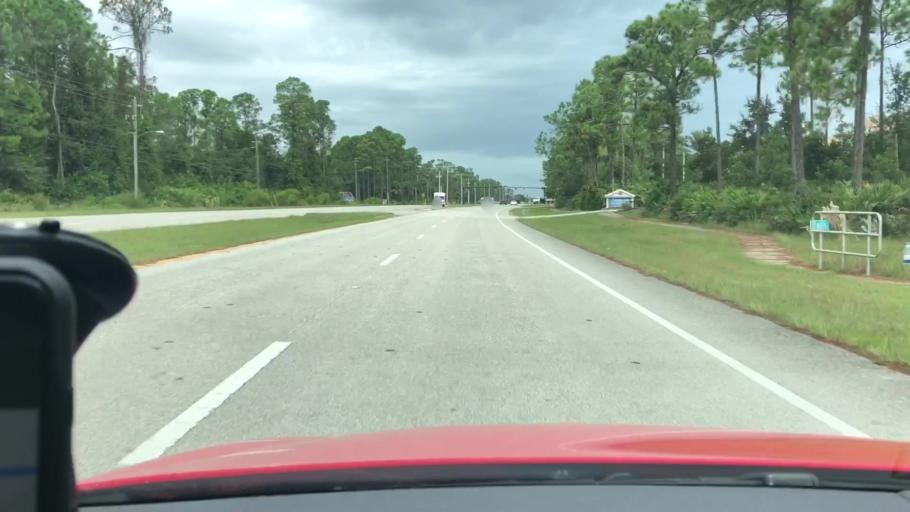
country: US
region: Florida
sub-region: Volusia County
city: Daytona Beach
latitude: 29.1987
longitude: -81.0862
